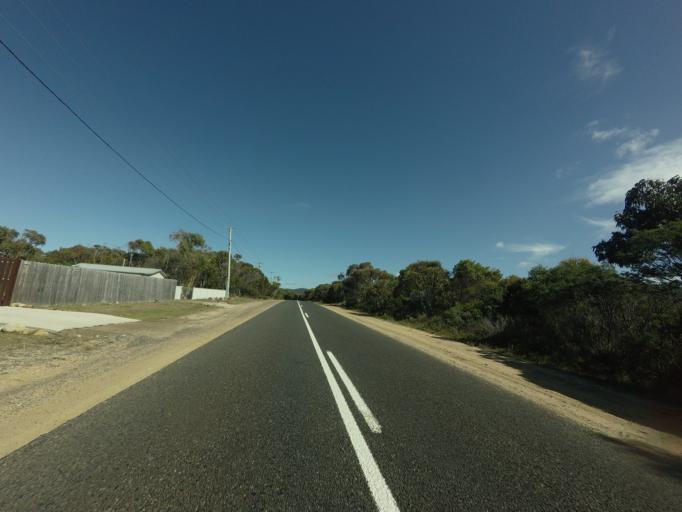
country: AU
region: Tasmania
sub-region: Break O'Day
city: St Helens
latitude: -41.8180
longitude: 148.2627
